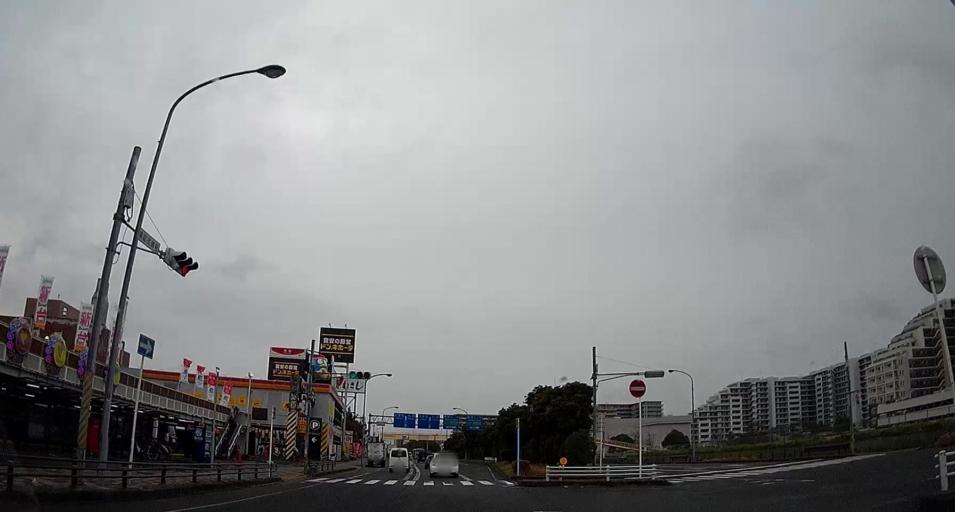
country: JP
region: Chiba
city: Funabashi
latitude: 35.6633
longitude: 140.0428
